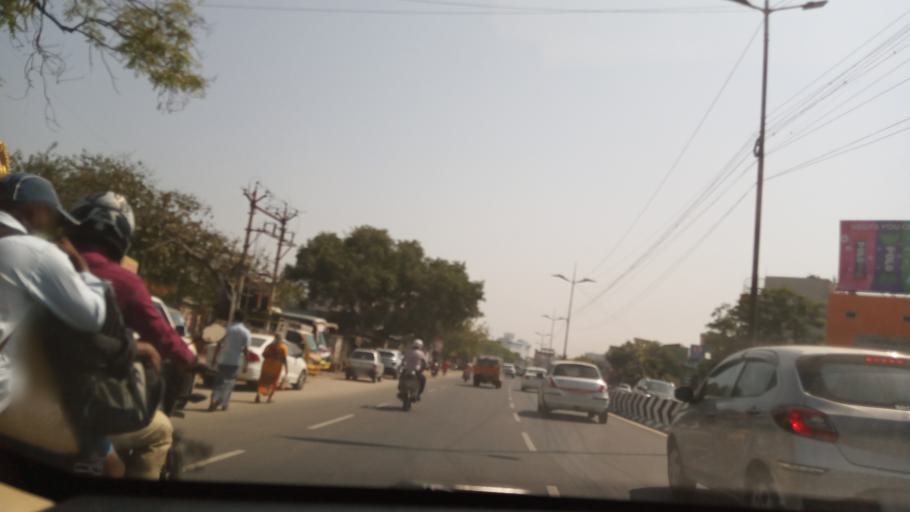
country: IN
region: Tamil Nadu
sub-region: Coimbatore
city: Irugur
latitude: 11.0540
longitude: 77.0632
